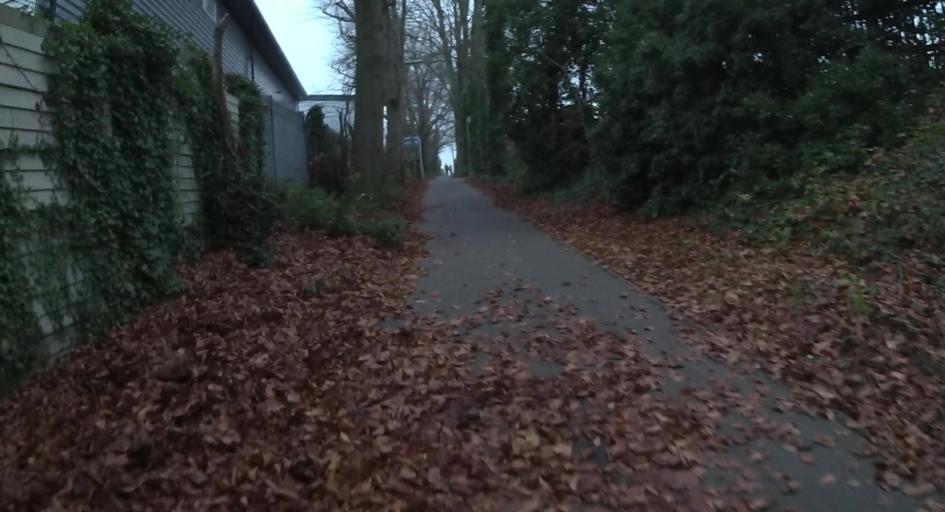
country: GB
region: England
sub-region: Hampshire
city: Kings Worthy
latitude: 51.0687
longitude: -1.2947
